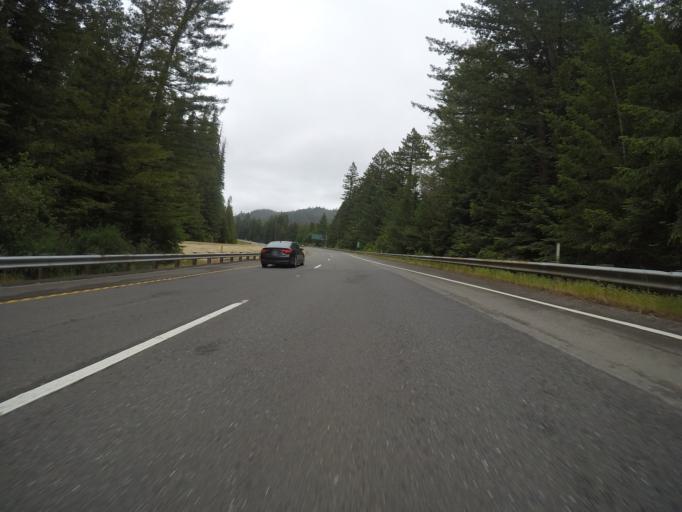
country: US
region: California
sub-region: Humboldt County
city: Rio Dell
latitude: 40.4403
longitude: -124.0368
